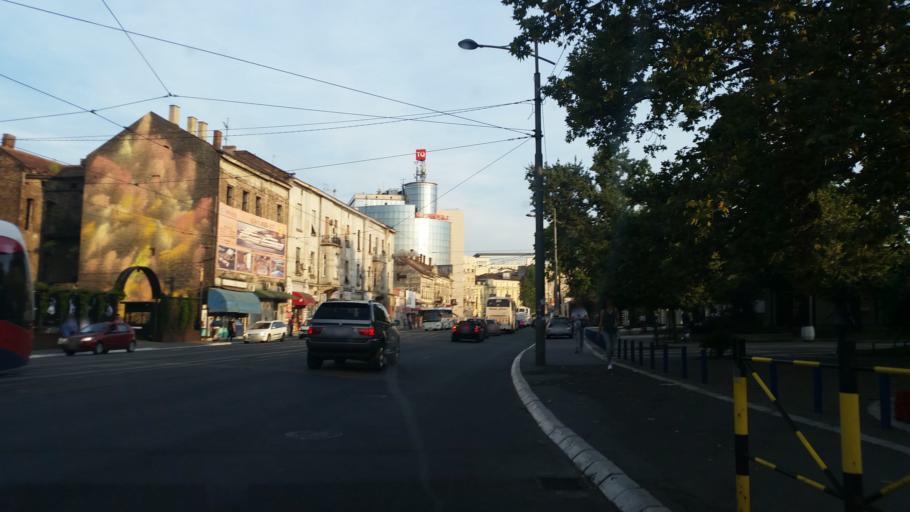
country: RS
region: Central Serbia
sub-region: Belgrade
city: Stari Grad
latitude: 44.8108
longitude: 20.4547
